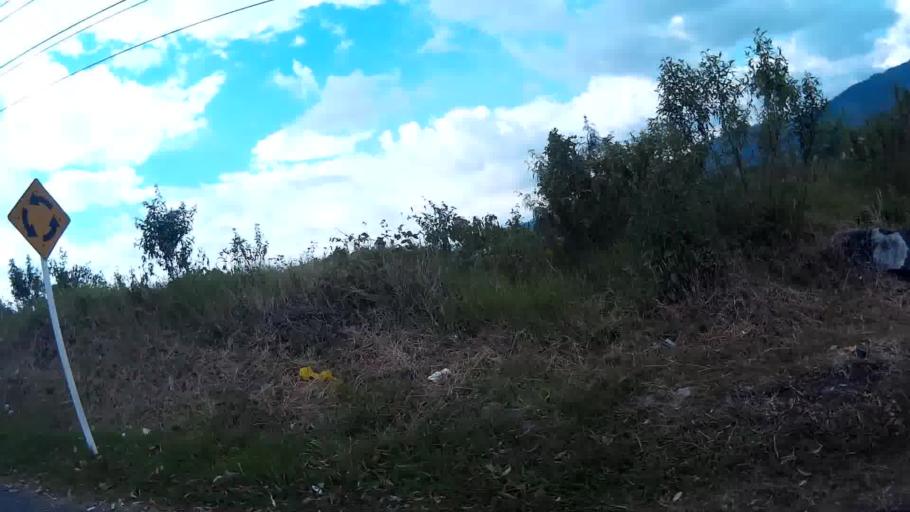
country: CO
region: Quindio
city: Calarca
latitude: 4.5621
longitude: -75.6510
